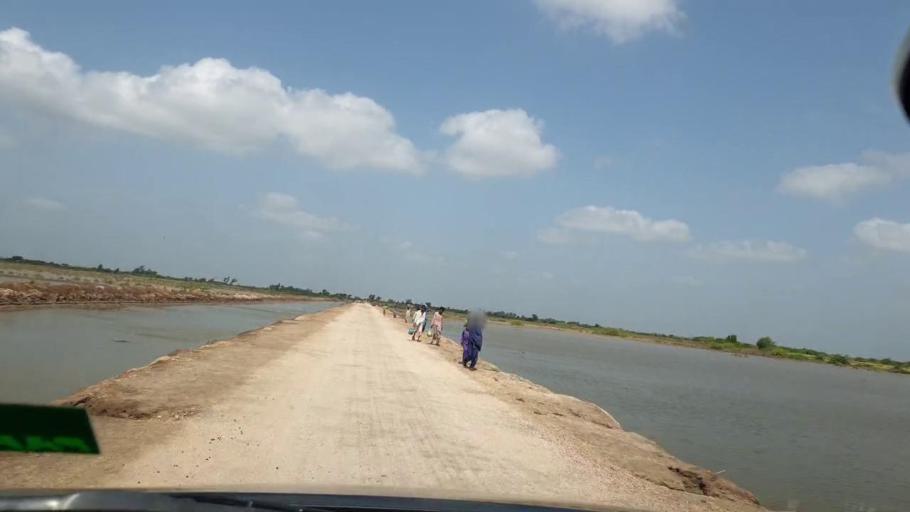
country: PK
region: Sindh
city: Kadhan
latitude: 24.5966
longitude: 69.1291
